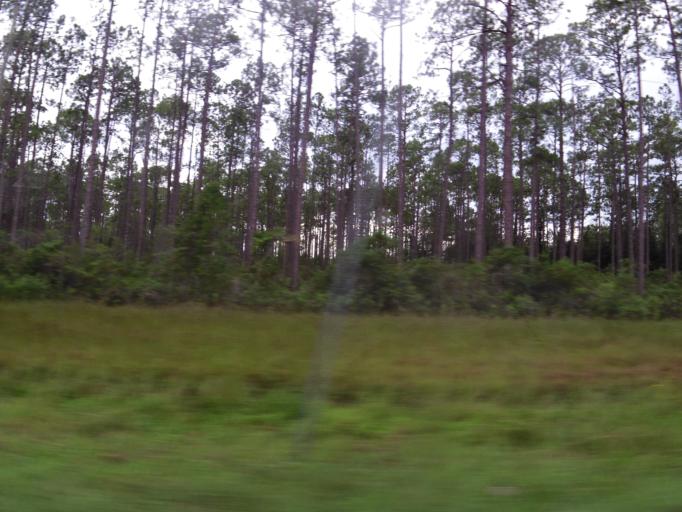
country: US
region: Florida
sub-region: Duval County
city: Baldwin
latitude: 30.4020
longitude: -82.0120
